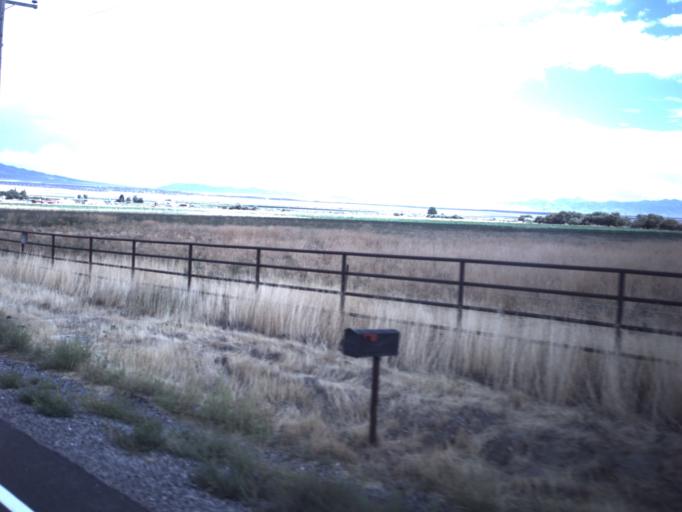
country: US
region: Utah
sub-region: Tooele County
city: Tooele
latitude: 40.3366
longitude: -112.4547
